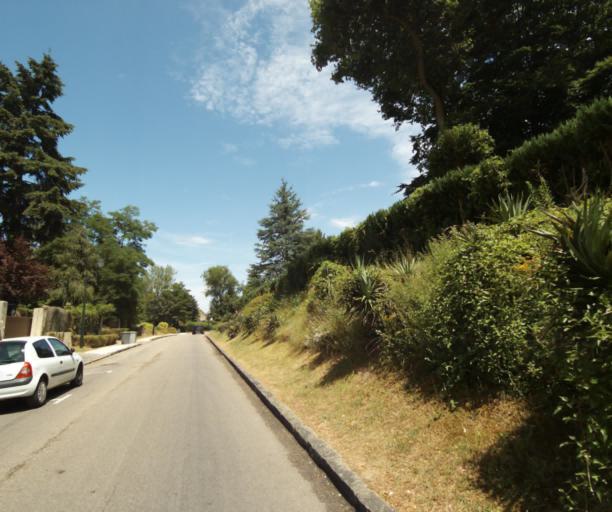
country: FR
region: Ile-de-France
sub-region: Departement de Seine-et-Marne
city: Cely
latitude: 48.4525
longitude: 2.5514
